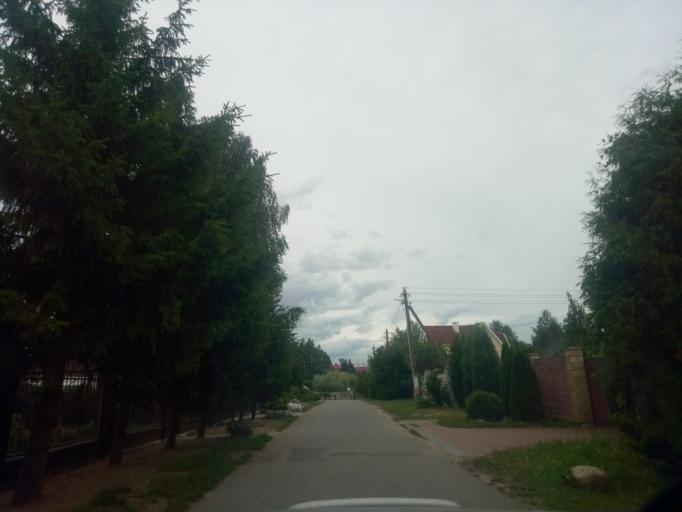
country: BY
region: Minsk
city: Zhdanovichy
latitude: 53.9172
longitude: 27.3957
